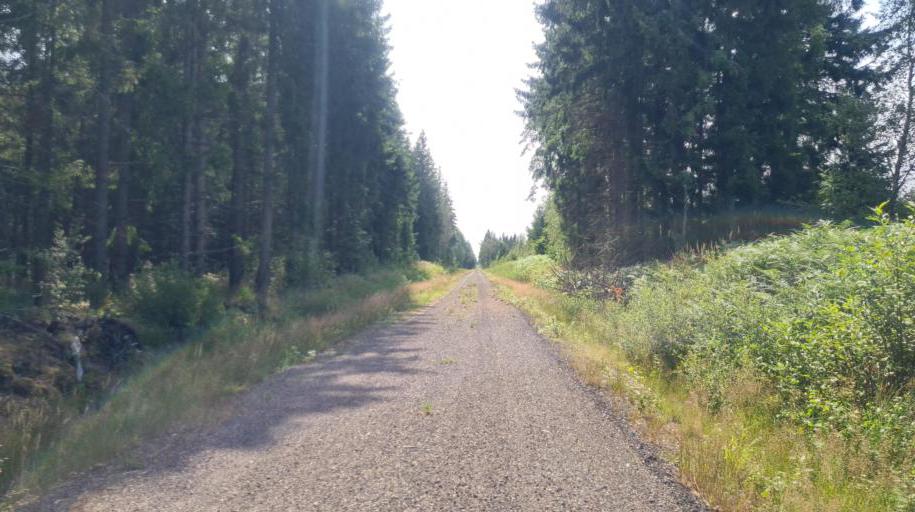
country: SE
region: Kronoberg
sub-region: Ljungby Kommun
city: Lagan
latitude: 56.9837
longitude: 13.9446
